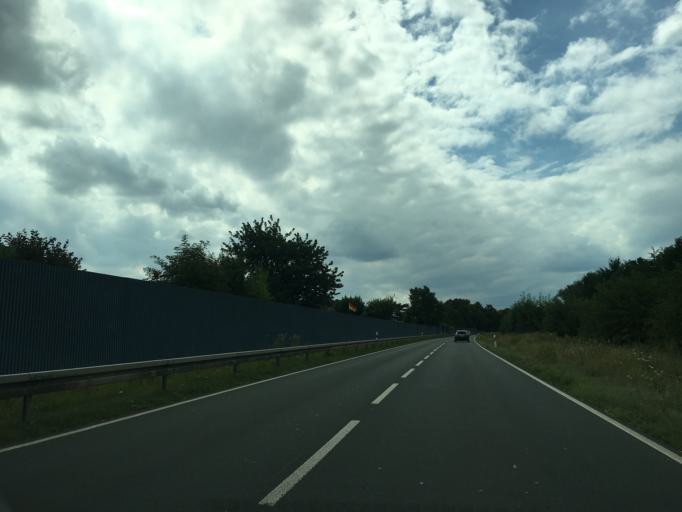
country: DE
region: North Rhine-Westphalia
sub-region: Regierungsbezirk Munster
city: Ascheberg
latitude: 51.7938
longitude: 7.6123
